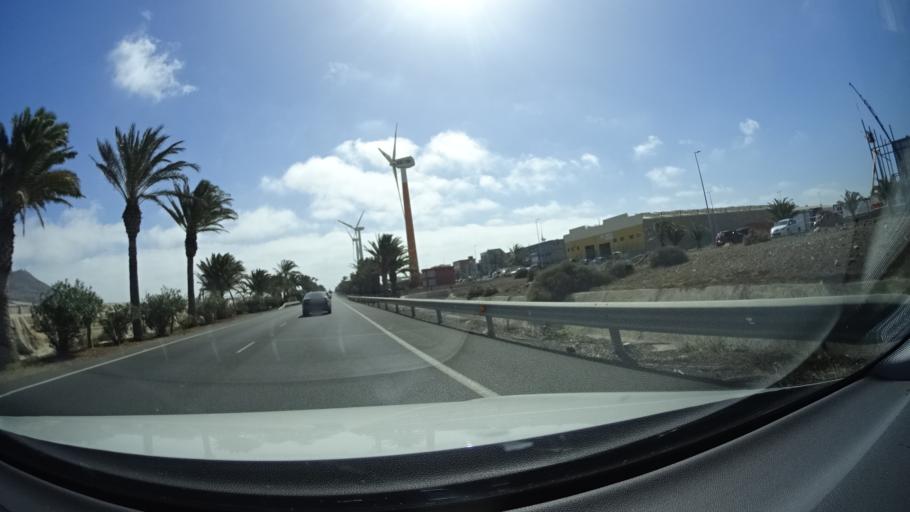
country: ES
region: Canary Islands
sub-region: Provincia de Las Palmas
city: Cruce de Arinaga
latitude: 27.8653
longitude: -15.4099
